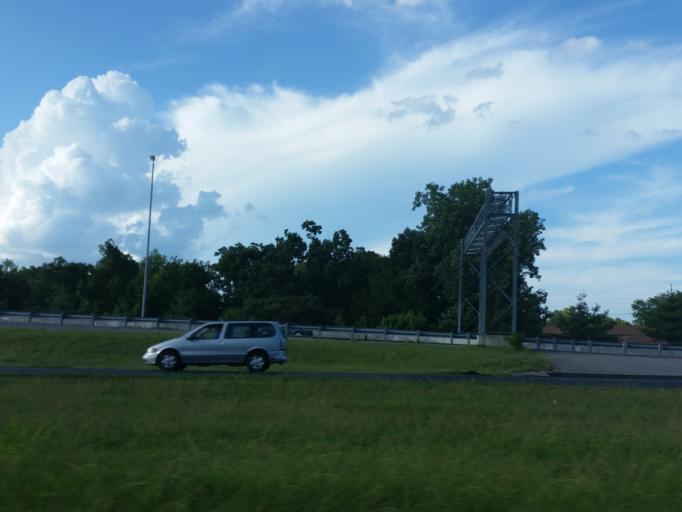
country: US
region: Tennessee
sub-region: Davidson County
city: Nashville
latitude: 36.2377
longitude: -86.7362
